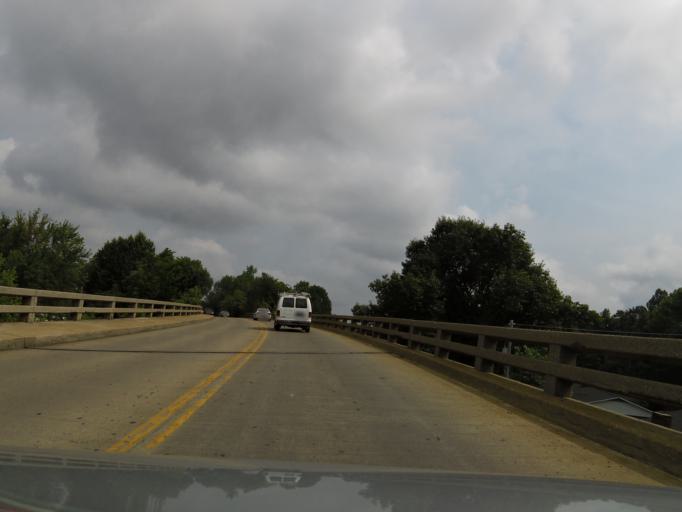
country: US
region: Kentucky
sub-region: Hopkins County
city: Madisonville
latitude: 37.3376
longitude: -87.4972
